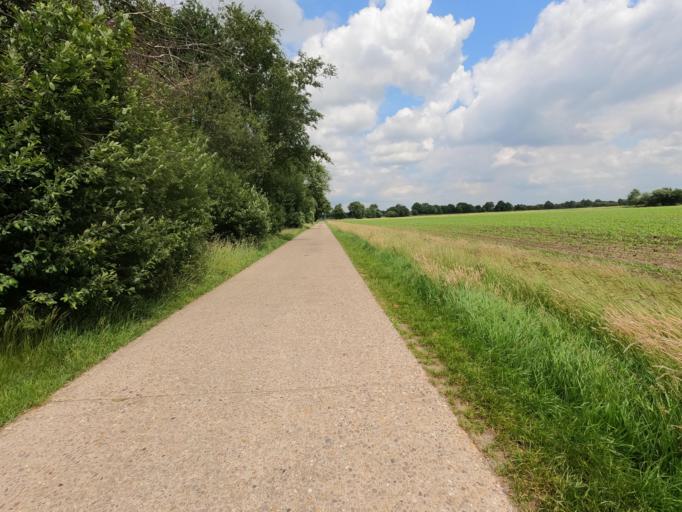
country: BE
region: Flanders
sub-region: Provincie Antwerpen
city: Kalmthout
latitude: 51.4160
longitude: 4.5132
